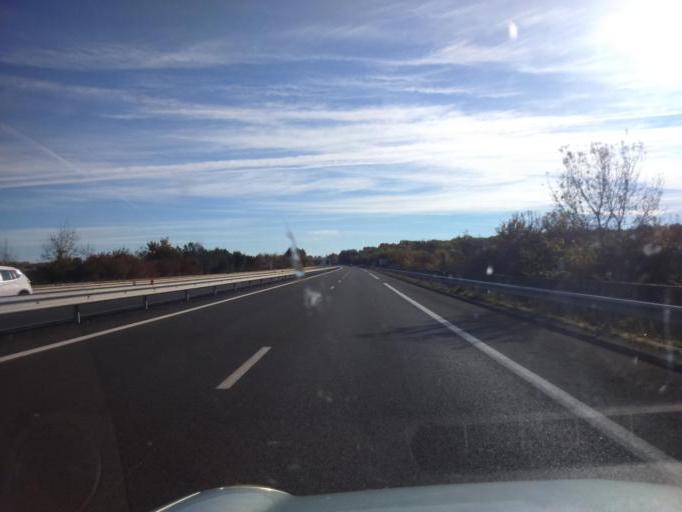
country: FR
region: Poitou-Charentes
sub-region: Departement de la Charente-Maritime
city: Tonnay-Charente
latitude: 45.9556
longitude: -0.9072
